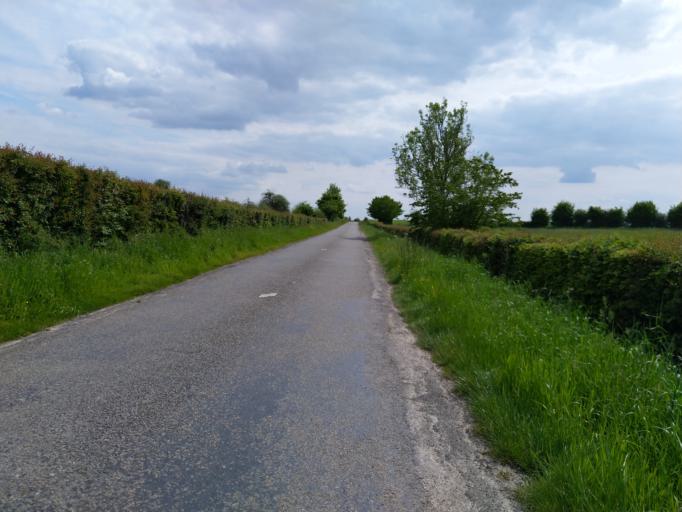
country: FR
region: Picardie
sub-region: Departement de l'Aisne
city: Boue
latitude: 50.0312
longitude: 3.6797
